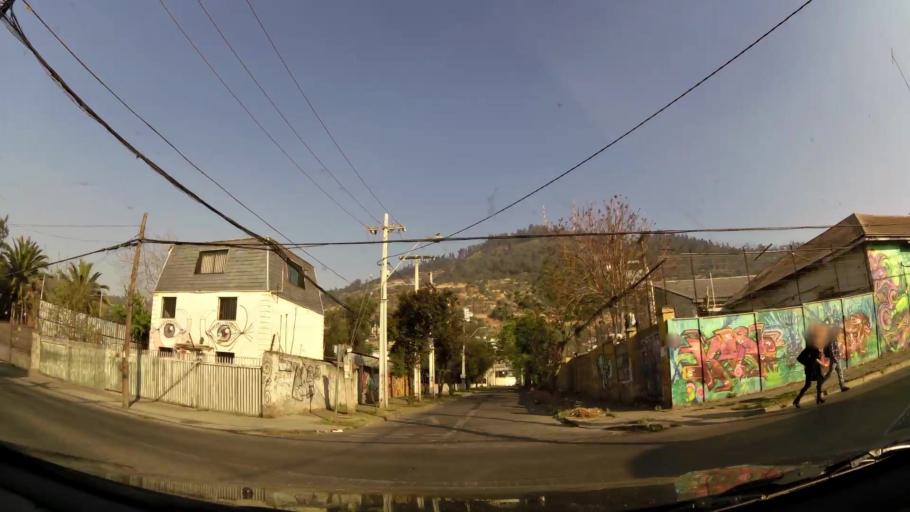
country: CL
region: Santiago Metropolitan
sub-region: Provincia de Santiago
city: Santiago
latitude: -33.4122
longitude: -70.6345
